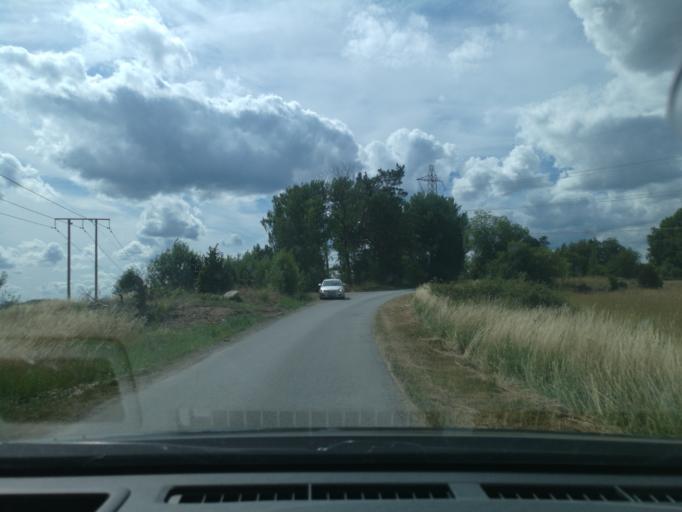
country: SE
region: Stockholm
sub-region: Sigtuna Kommun
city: Marsta
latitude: 59.6641
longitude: 17.8678
